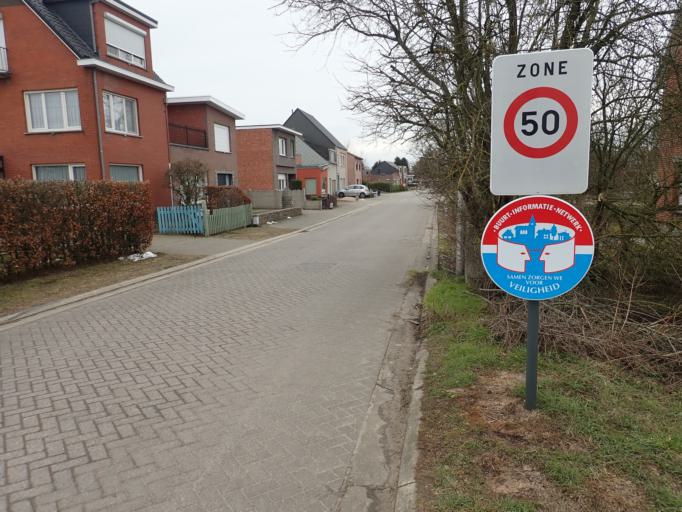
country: BE
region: Flanders
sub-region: Provincie Antwerpen
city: Nijlen
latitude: 51.1618
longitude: 4.6929
